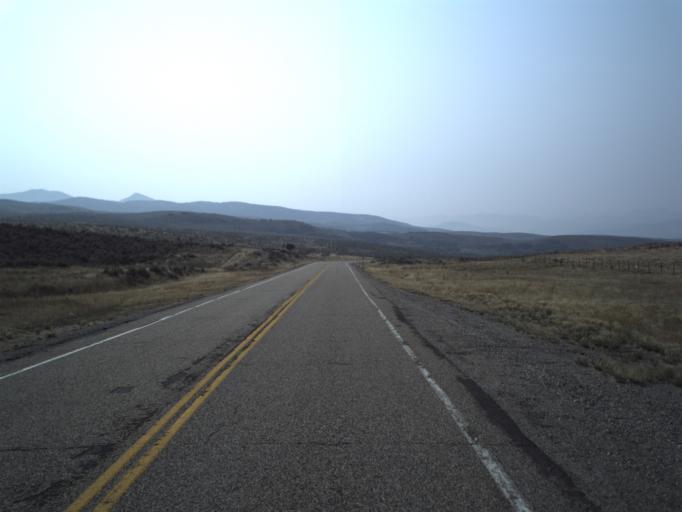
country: US
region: Utah
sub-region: Morgan County
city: Morgan
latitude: 40.9534
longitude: -111.5496
